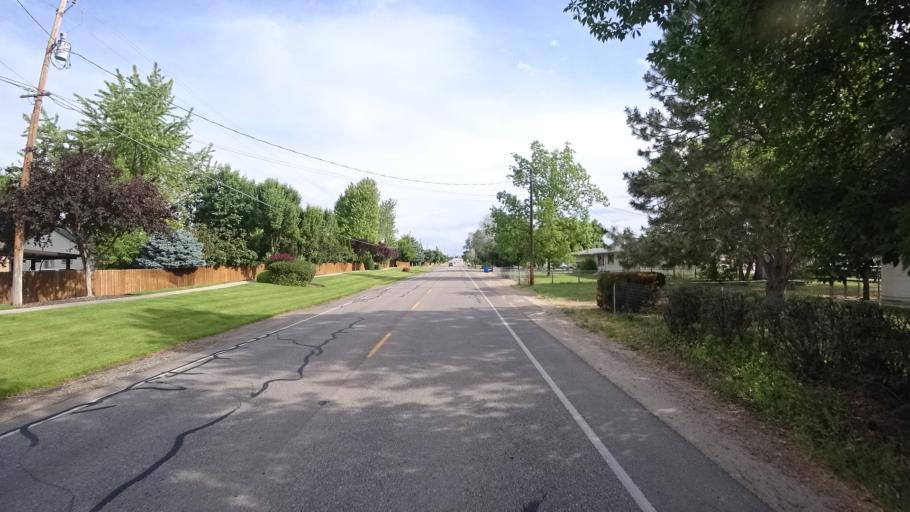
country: US
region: Idaho
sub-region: Ada County
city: Meridian
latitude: 43.5841
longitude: -116.3746
